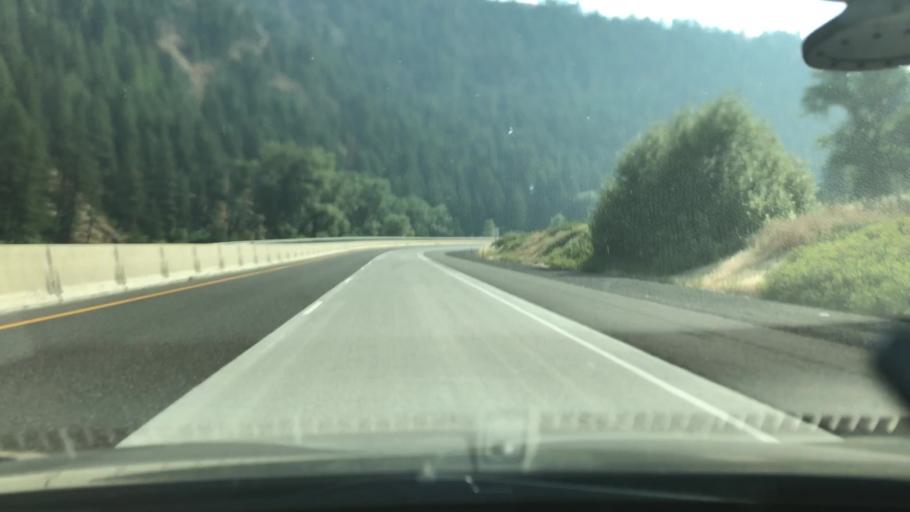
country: US
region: Oregon
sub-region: Union County
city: La Grande
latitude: 45.3495
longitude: -118.1995
